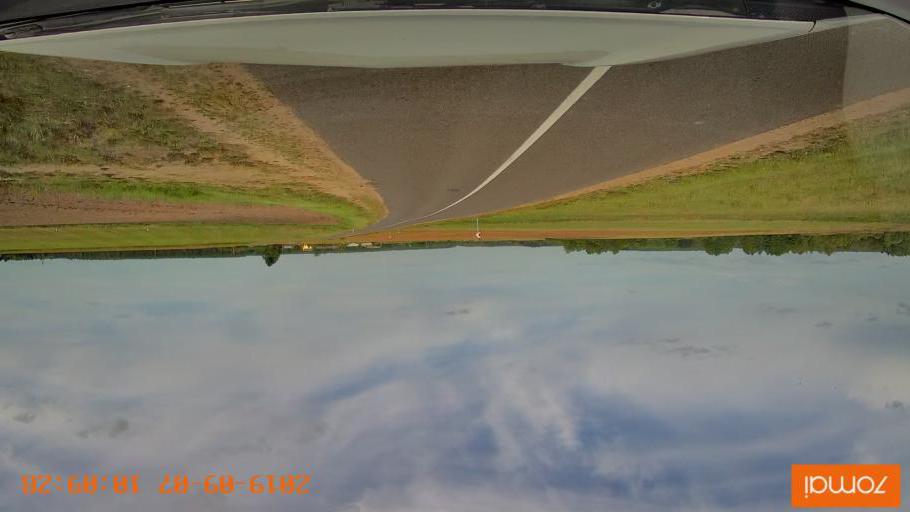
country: BY
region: Grodnenskaya
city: Voranava
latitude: 54.0956
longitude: 25.3736
